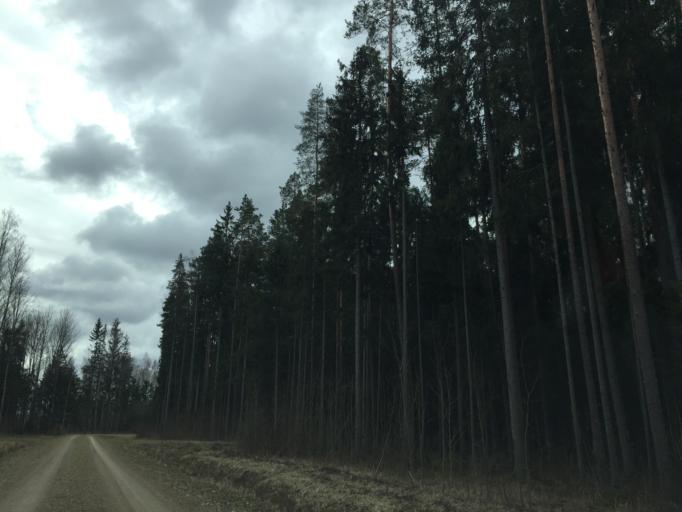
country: LV
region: Akniste
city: Akniste
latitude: 56.0774
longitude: 25.7618
